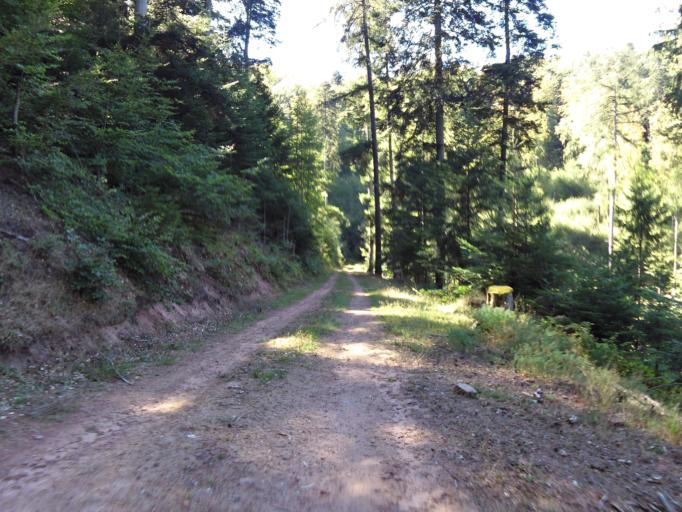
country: DE
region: Rheinland-Pfalz
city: Esthal
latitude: 49.3967
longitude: 7.9814
